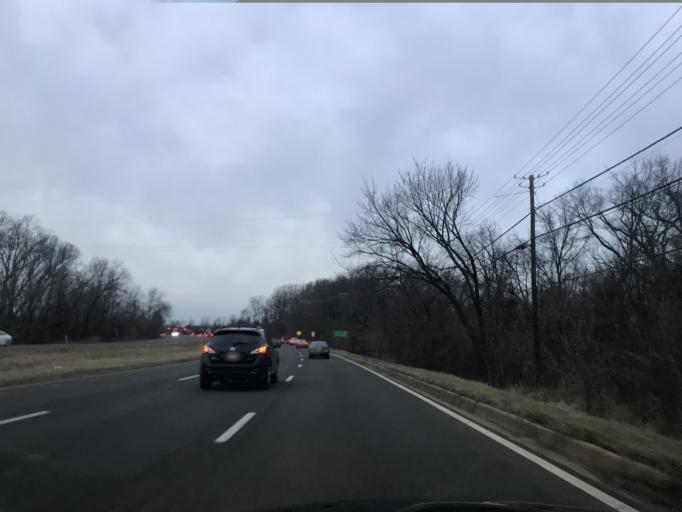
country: US
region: Maryland
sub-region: Prince George's County
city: Lake Arbor
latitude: 38.9095
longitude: -76.8352
